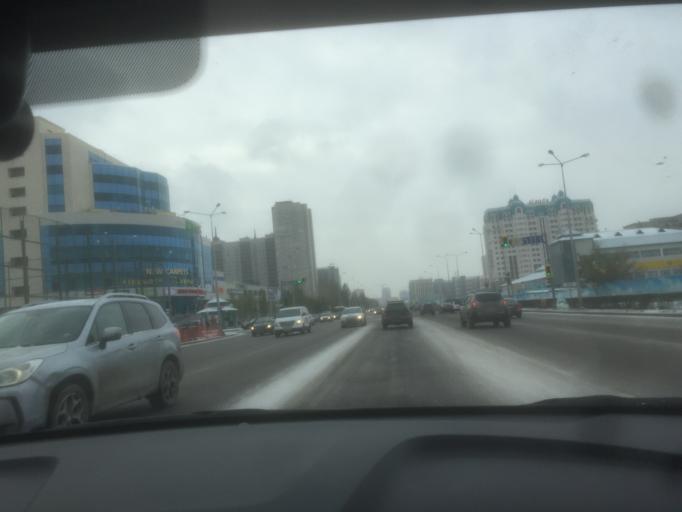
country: KZ
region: Astana Qalasy
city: Astana
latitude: 51.1423
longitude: 71.4627
